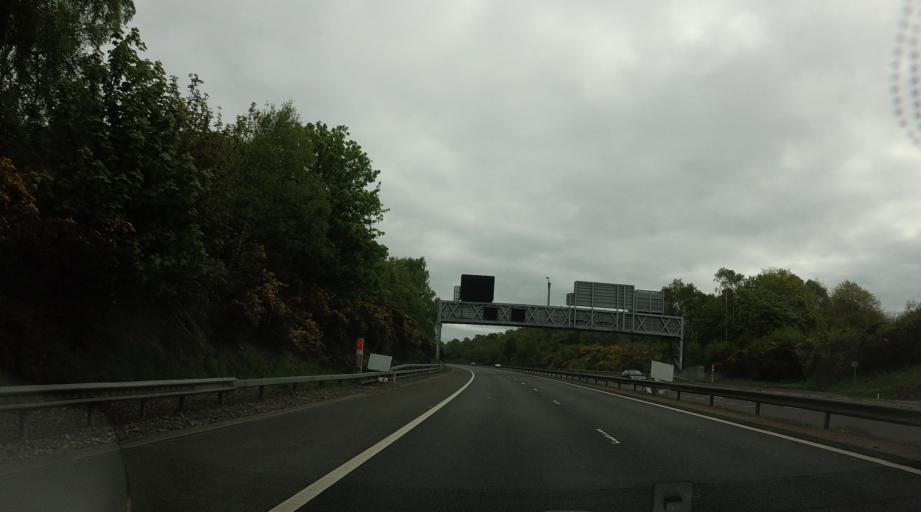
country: GB
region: Scotland
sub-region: Fife
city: Inverkeithing
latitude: 56.0502
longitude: -3.3914
